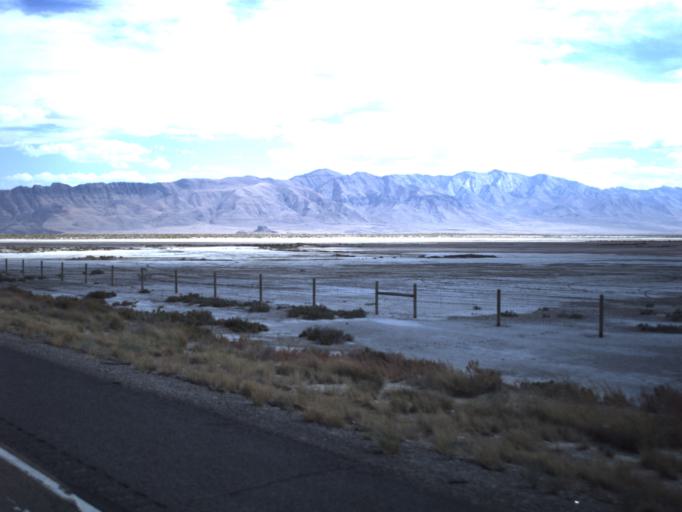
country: US
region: Utah
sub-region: Tooele County
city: Grantsville
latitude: 40.7561
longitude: -112.7580
